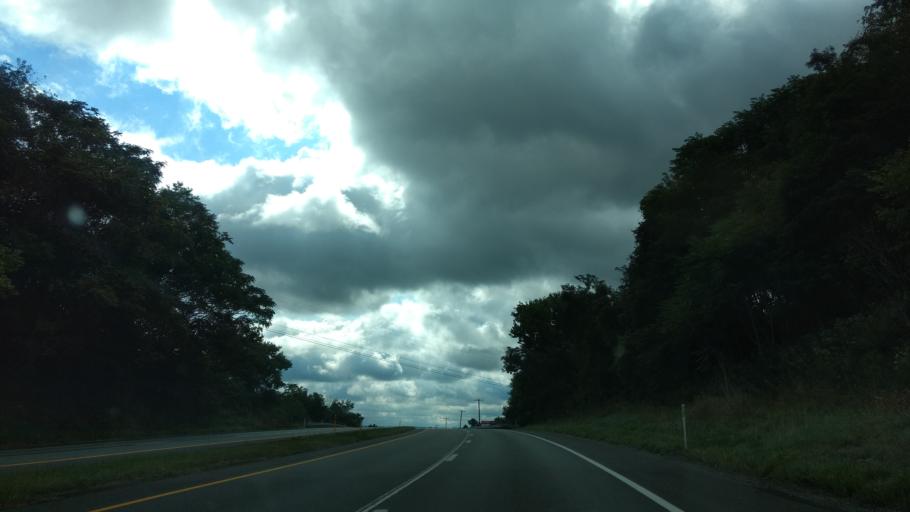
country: US
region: Pennsylvania
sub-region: Westmoreland County
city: Fellsburg
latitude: 40.1744
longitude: -79.8017
